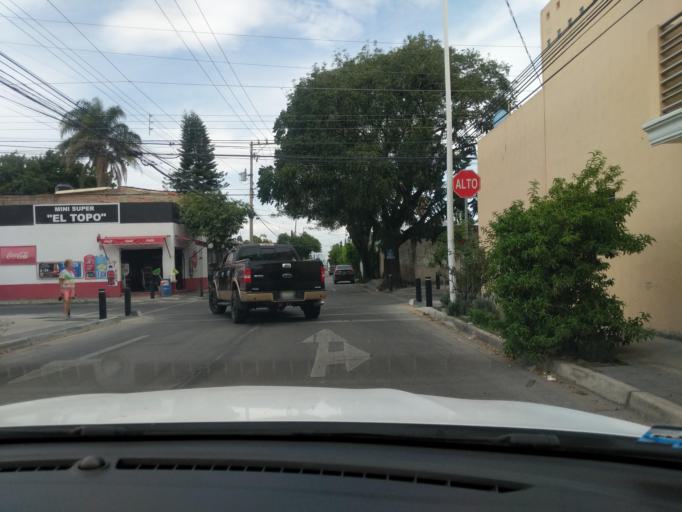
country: MX
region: Jalisco
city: Nuevo Mexico
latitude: 20.7590
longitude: -103.4373
